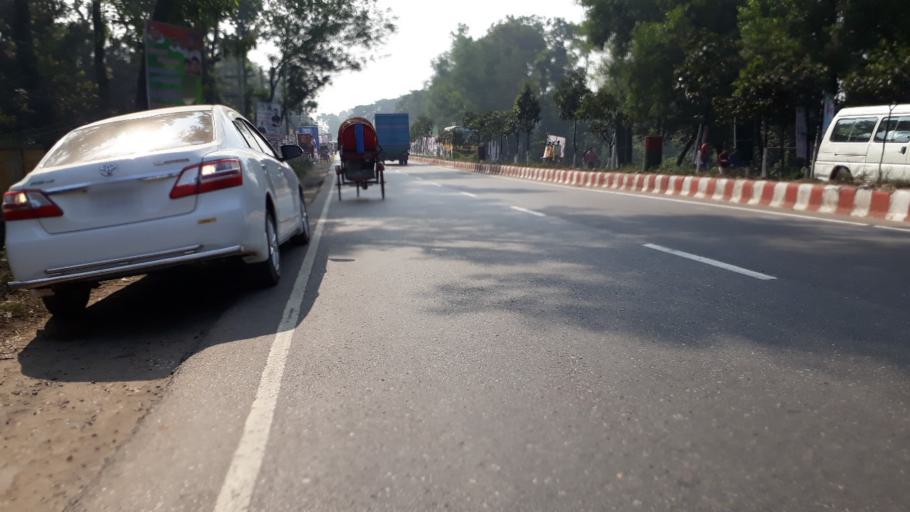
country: BD
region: Dhaka
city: Tungi
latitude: 23.8739
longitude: 90.2734
